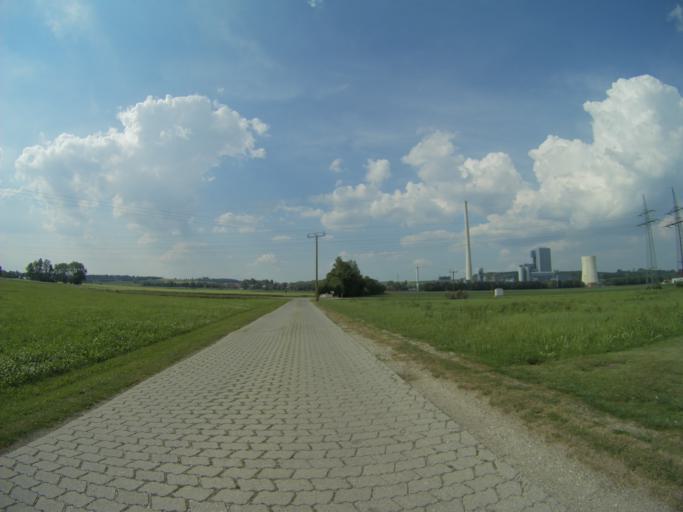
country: DE
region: Bavaria
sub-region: Upper Bavaria
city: Zolling
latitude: 48.4477
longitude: 11.7982
